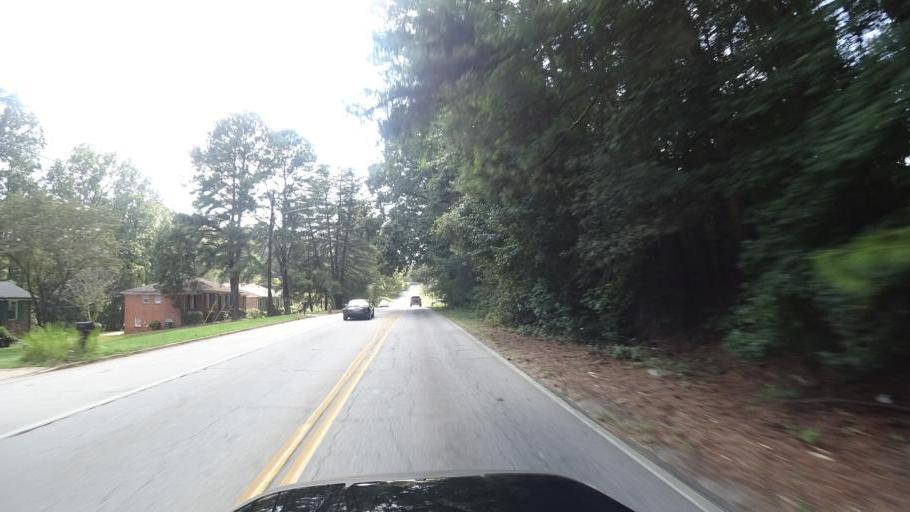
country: US
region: Georgia
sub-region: DeKalb County
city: Stone Mountain
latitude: 33.7894
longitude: -84.1845
